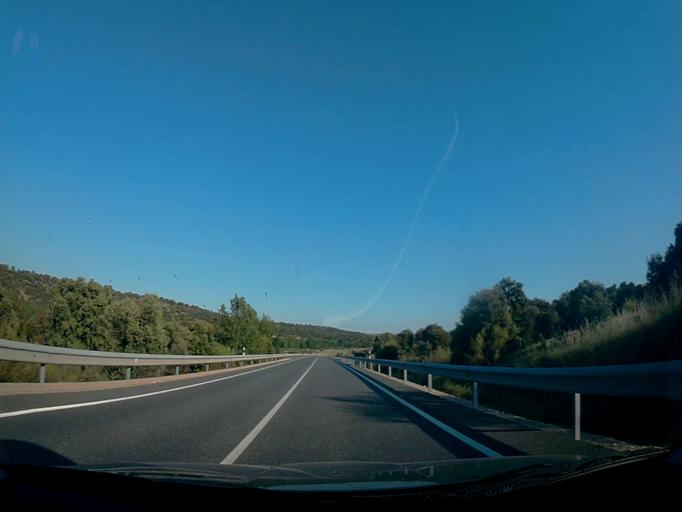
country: ES
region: Castille-La Mancha
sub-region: Province of Toledo
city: Escalona
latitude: 40.1855
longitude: -4.4026
